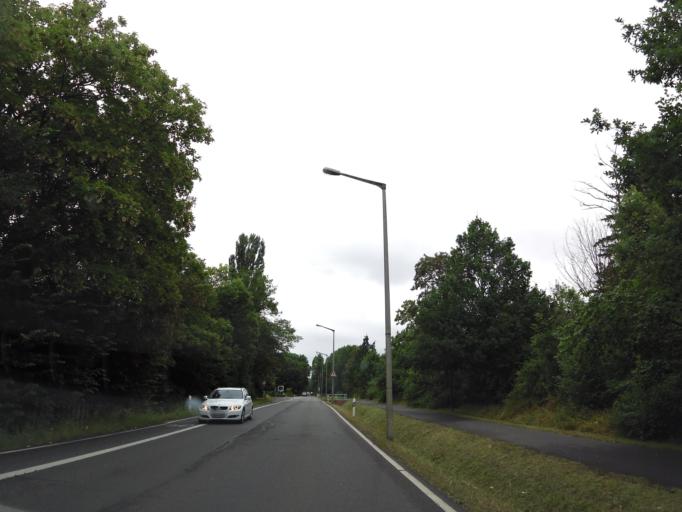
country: DE
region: Saxony
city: Markkleeberg
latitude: 51.2905
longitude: 12.4285
